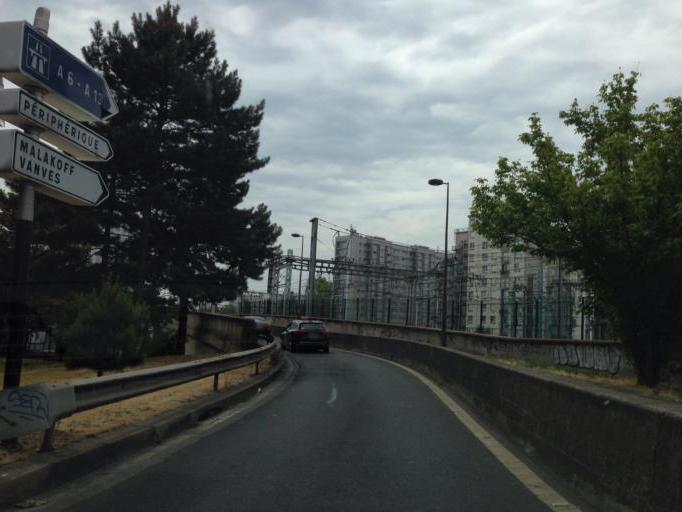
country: FR
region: Ile-de-France
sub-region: Departement des Hauts-de-Seine
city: Malakoff
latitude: 48.8288
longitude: 2.3059
